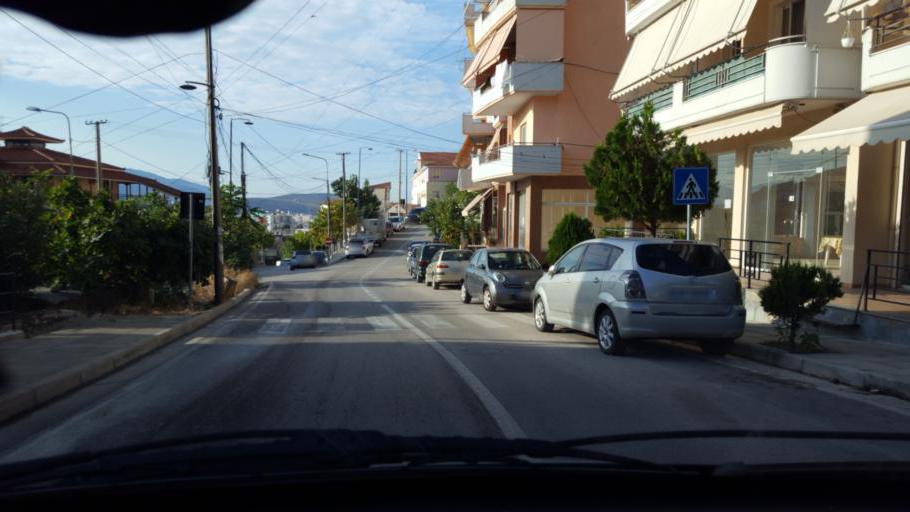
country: AL
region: Vlore
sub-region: Rrethi i Sarandes
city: Sarande
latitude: 39.8767
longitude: 20.0006
